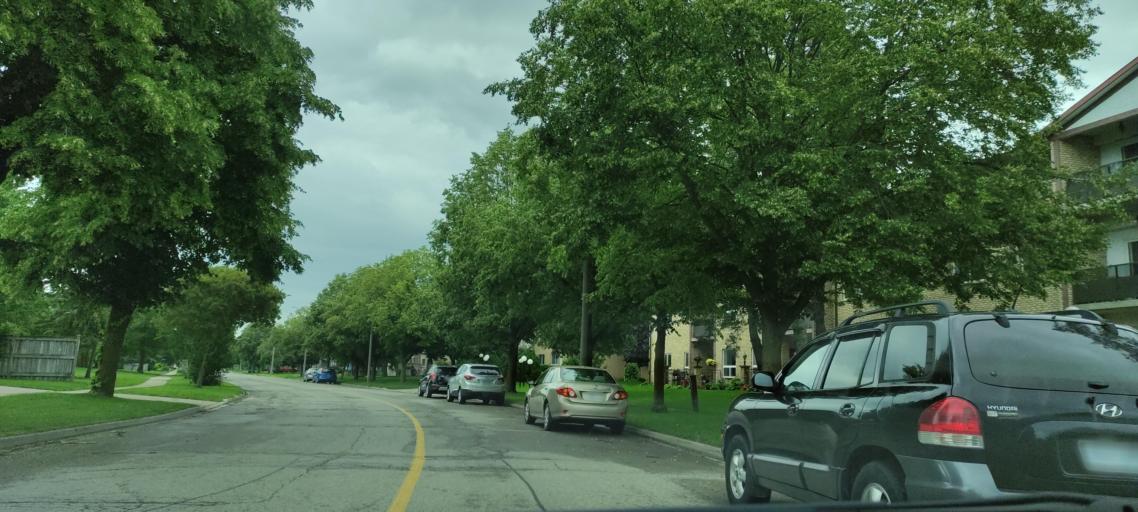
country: CA
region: Ontario
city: Stratford
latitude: 43.3822
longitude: -80.9765
